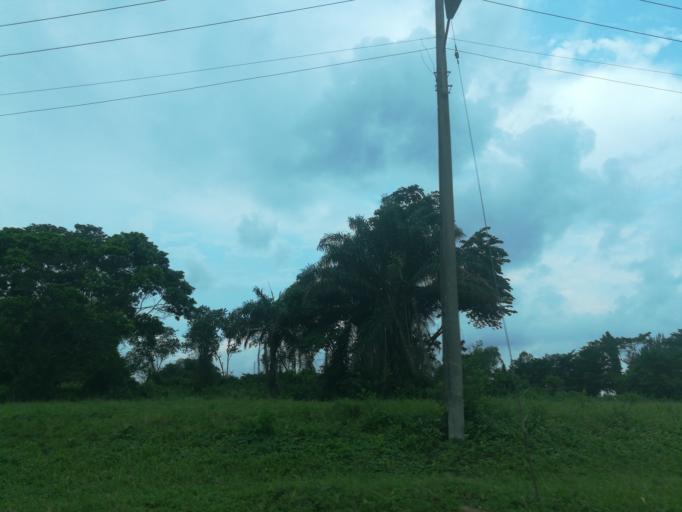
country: NG
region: Lagos
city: Ikorodu
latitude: 6.6355
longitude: 3.5227
